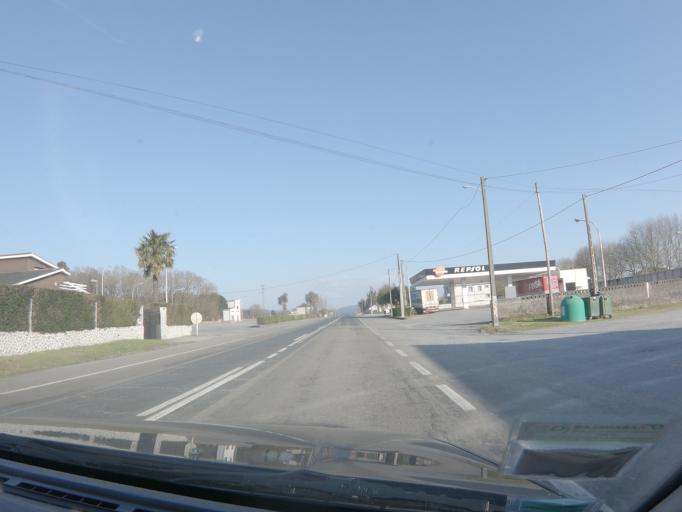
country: ES
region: Galicia
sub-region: Provincia de Lugo
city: Corgo
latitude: 42.9451
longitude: -7.4374
